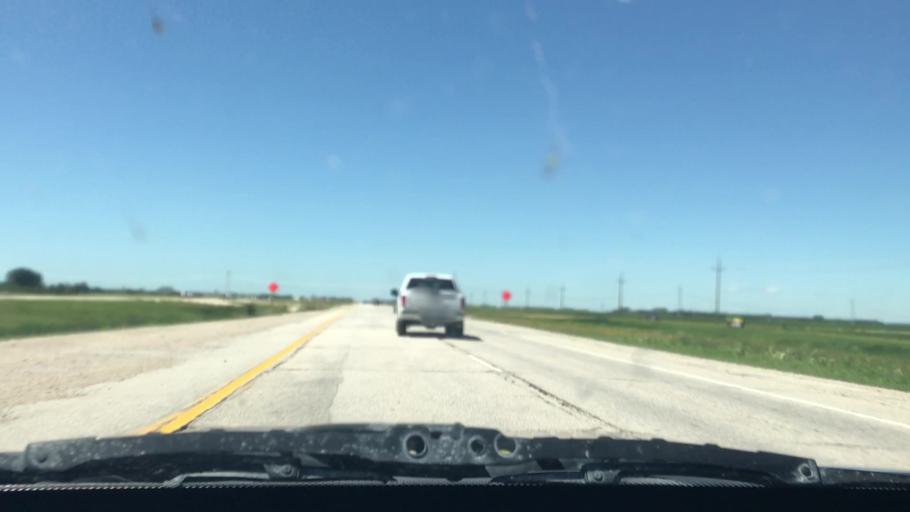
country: CA
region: Manitoba
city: Steinbach
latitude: 49.7074
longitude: -96.6615
